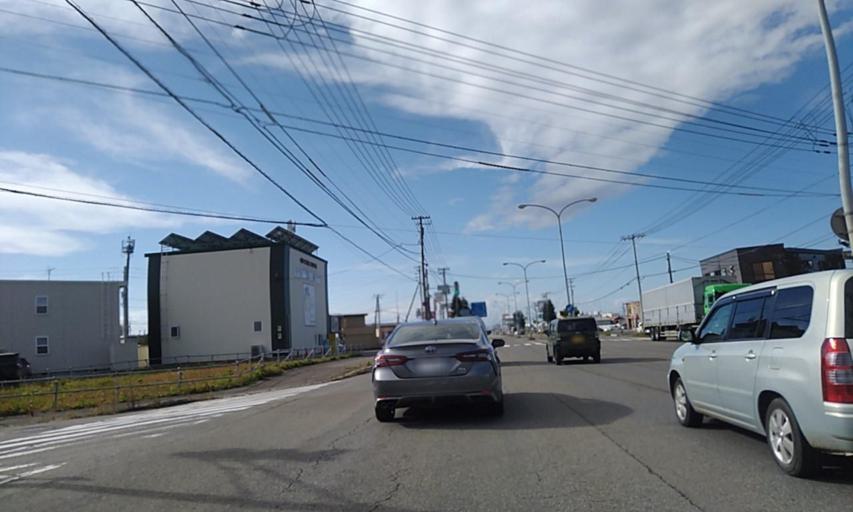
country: JP
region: Hokkaido
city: Obihiro
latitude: 42.9166
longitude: 143.2473
